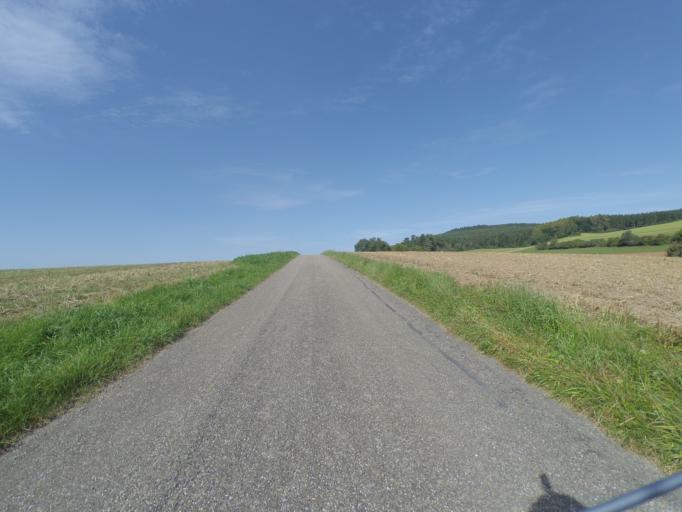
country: DE
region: Baden-Wuerttemberg
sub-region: Freiburg Region
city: Loffingen
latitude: 47.8549
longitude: 8.3419
